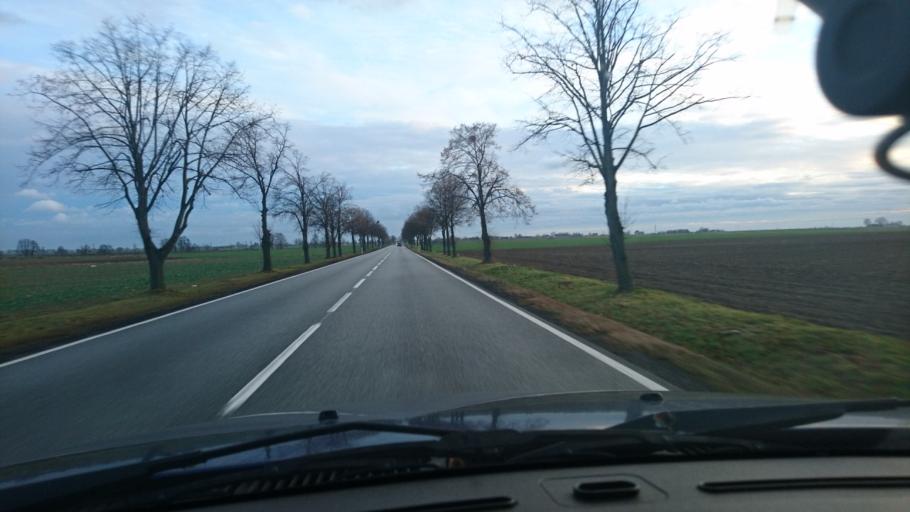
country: PL
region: Opole Voivodeship
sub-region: Powiat kluczborski
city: Kluczbork
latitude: 51.0219
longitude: 18.1948
